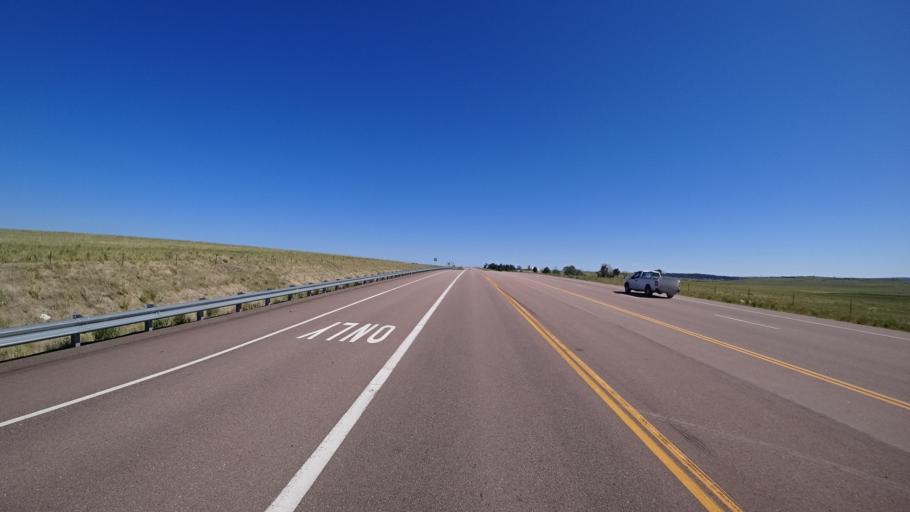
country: US
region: Colorado
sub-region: El Paso County
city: Cimarron Hills
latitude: 38.8279
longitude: -104.6827
